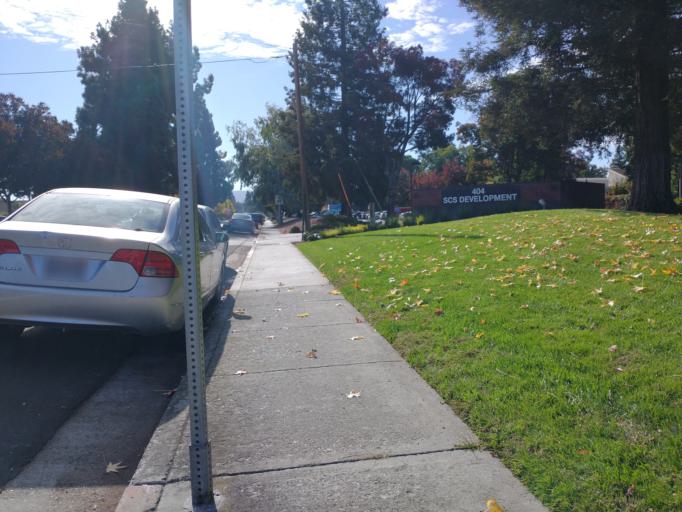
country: US
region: California
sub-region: Santa Clara County
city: Santa Clara
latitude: 37.3326
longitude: -121.9623
